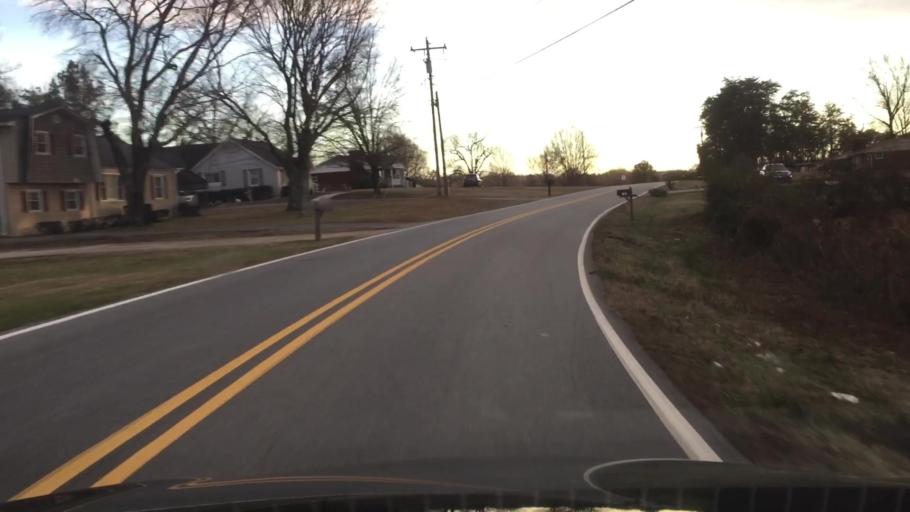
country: US
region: North Carolina
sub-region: Rockingham County
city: Reidsville
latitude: 36.4049
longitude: -79.6576
